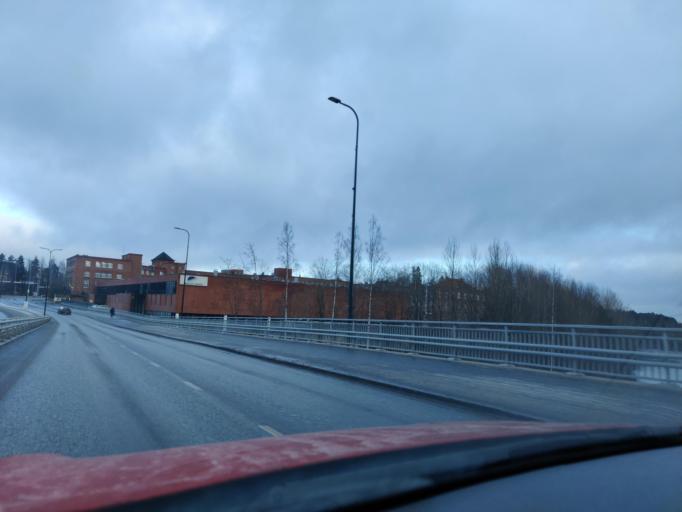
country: FI
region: Pirkanmaa
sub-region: Tampere
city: Nokia
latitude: 61.4726
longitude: 23.5056
